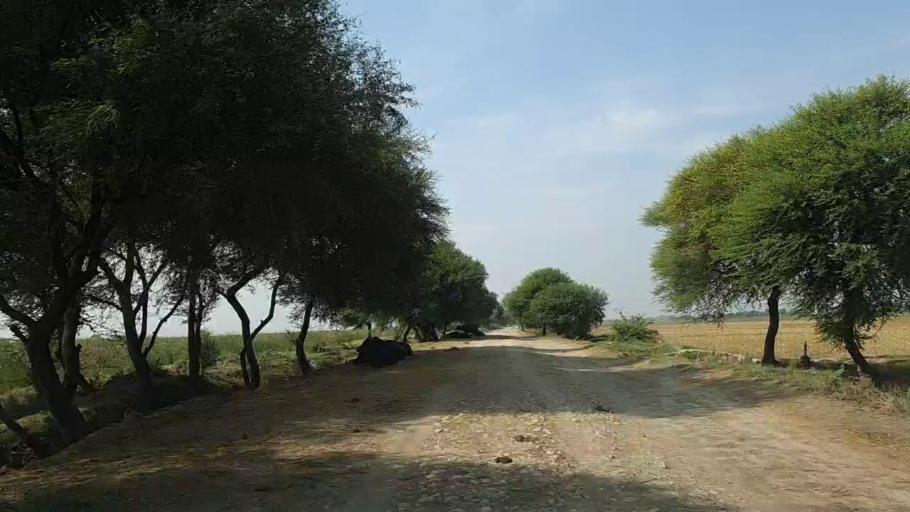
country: PK
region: Sindh
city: Mirpur Batoro
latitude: 24.6111
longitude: 68.2339
